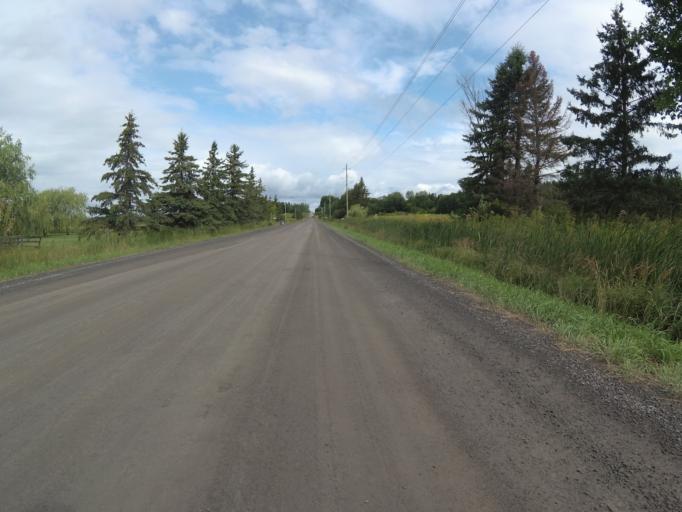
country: CA
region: Ontario
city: Clarence-Rockland
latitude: 45.4827
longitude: -75.3101
